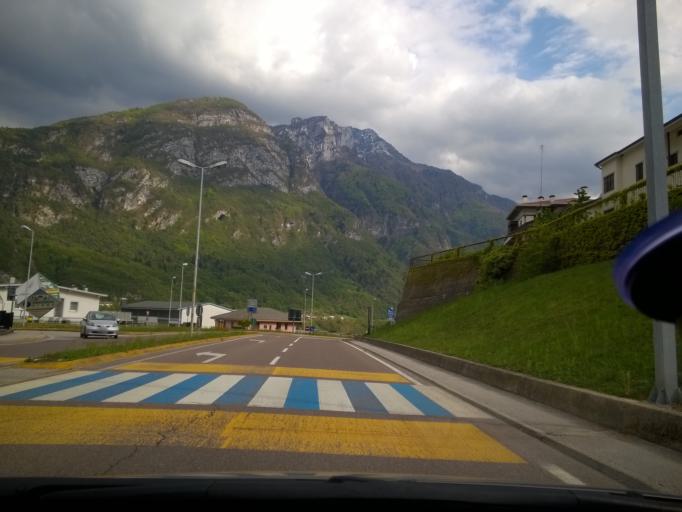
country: IT
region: Veneto
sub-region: Provincia di Belluno
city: Longarone
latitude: 46.2654
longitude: 12.3016
